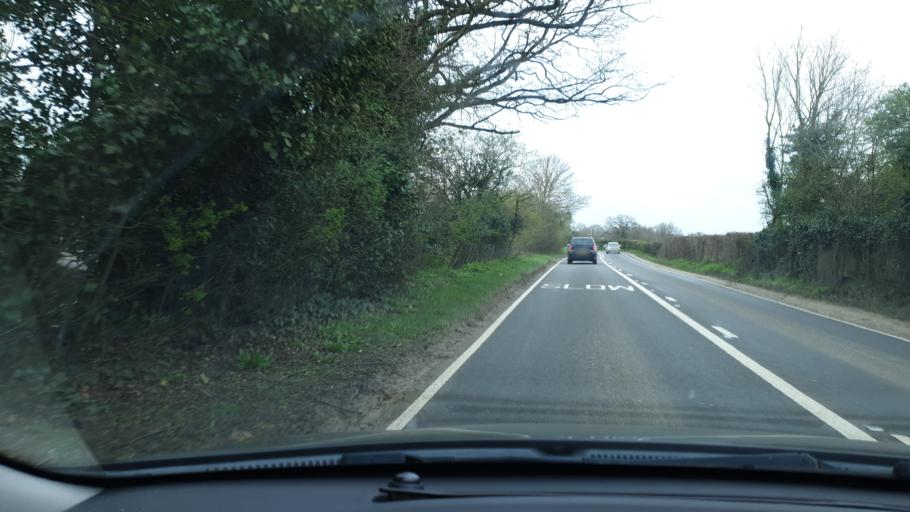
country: GB
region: England
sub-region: Essex
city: Great Horkesley
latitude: 51.9488
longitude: 0.8749
